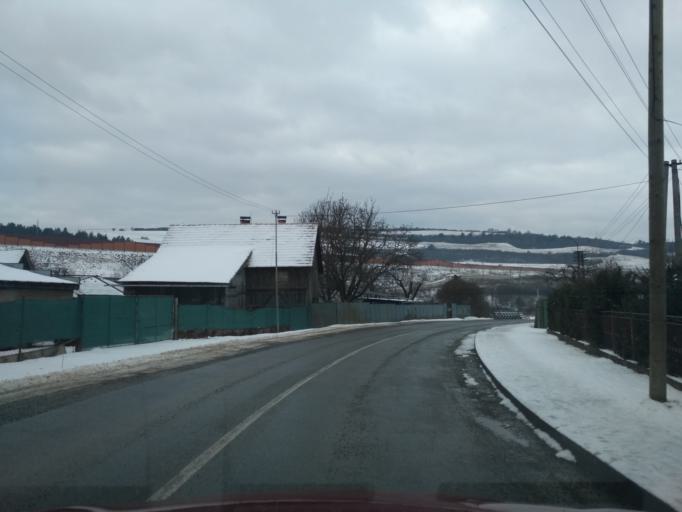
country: SK
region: Presovsky
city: Sabinov
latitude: 49.0019
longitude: 21.0779
